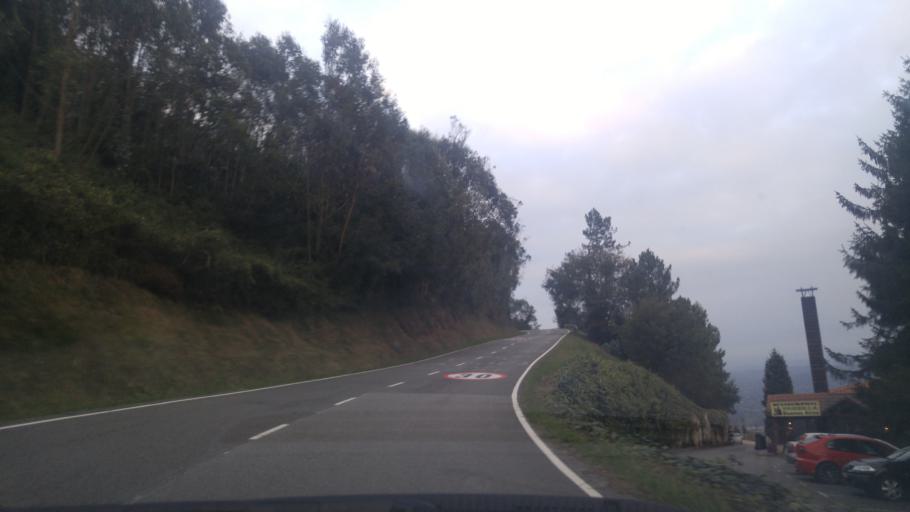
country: ES
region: Asturias
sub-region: Province of Asturias
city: Oviedo
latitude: 43.3823
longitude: -5.8558
